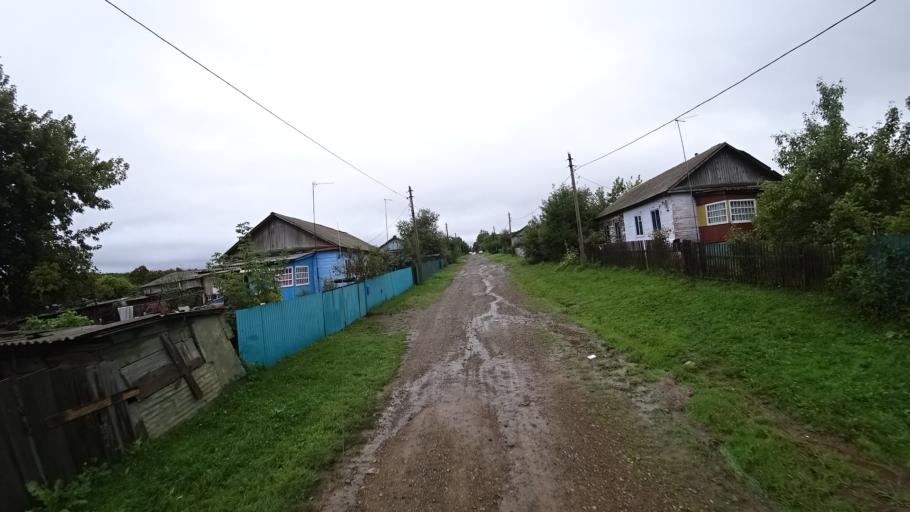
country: RU
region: Primorskiy
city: Monastyrishche
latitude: 44.2720
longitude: 132.4288
